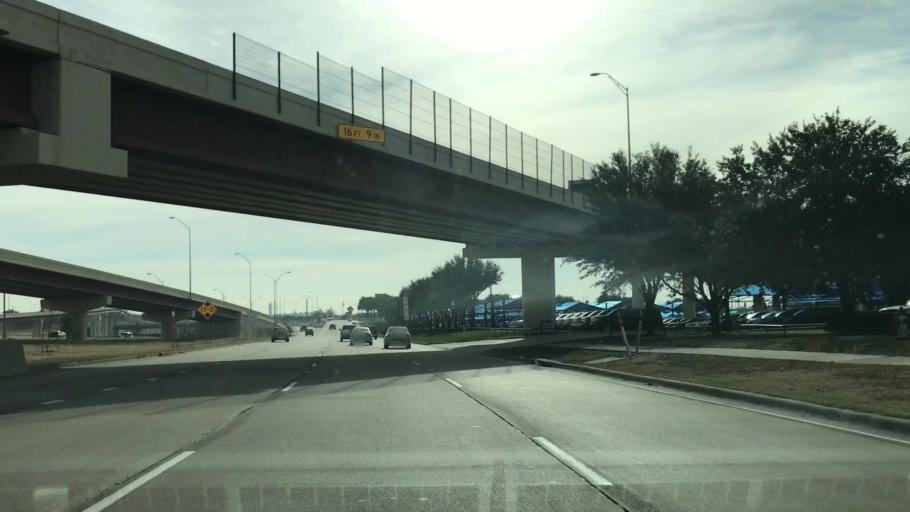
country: US
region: Texas
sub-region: Tarrant County
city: Grapevine
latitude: 32.9281
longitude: -97.0933
